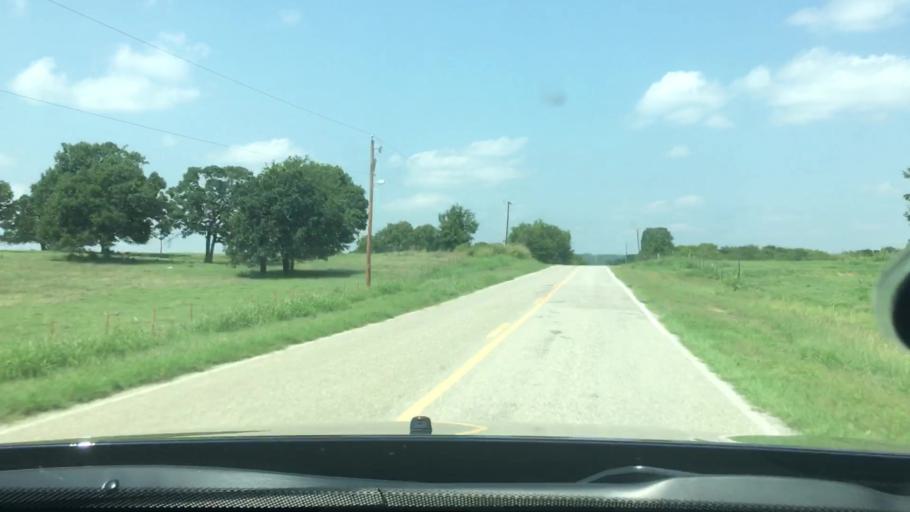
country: US
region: Oklahoma
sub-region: Johnston County
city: Tishomingo
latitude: 34.3960
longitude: -96.4962
